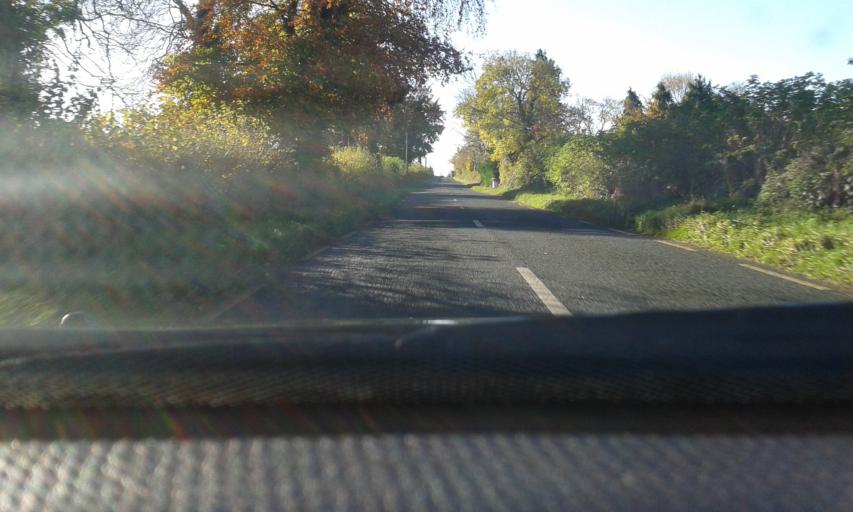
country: IE
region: Leinster
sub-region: Kildare
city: Rathangan
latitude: 53.1762
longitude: -7.0243
